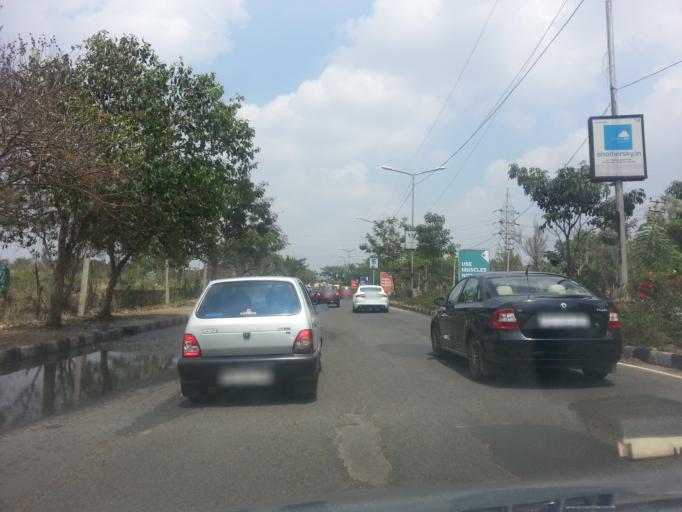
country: IN
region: Karnataka
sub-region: Bangalore Urban
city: Bangalore
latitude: 12.9437
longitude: 77.6387
